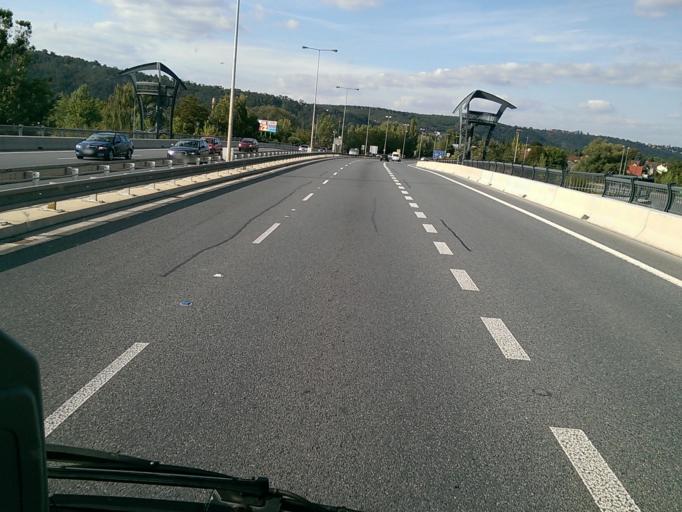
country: CZ
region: Praha
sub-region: Praha 12
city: Modrany
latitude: 49.9937
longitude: 14.3986
